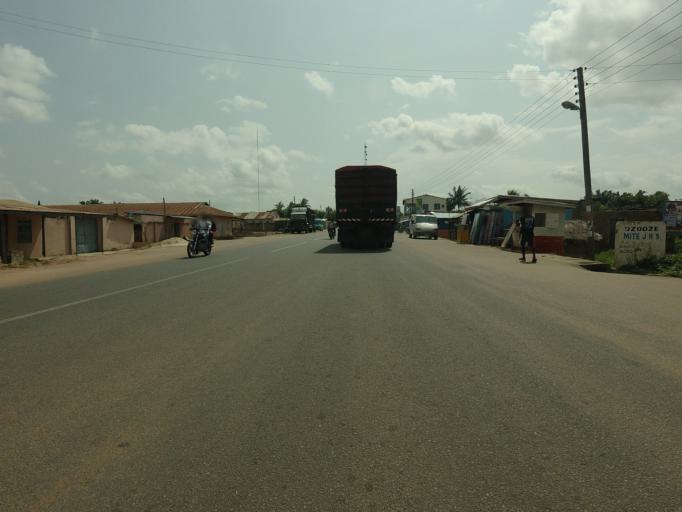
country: TG
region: Maritime
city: Lome
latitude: 6.2317
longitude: 1.0040
